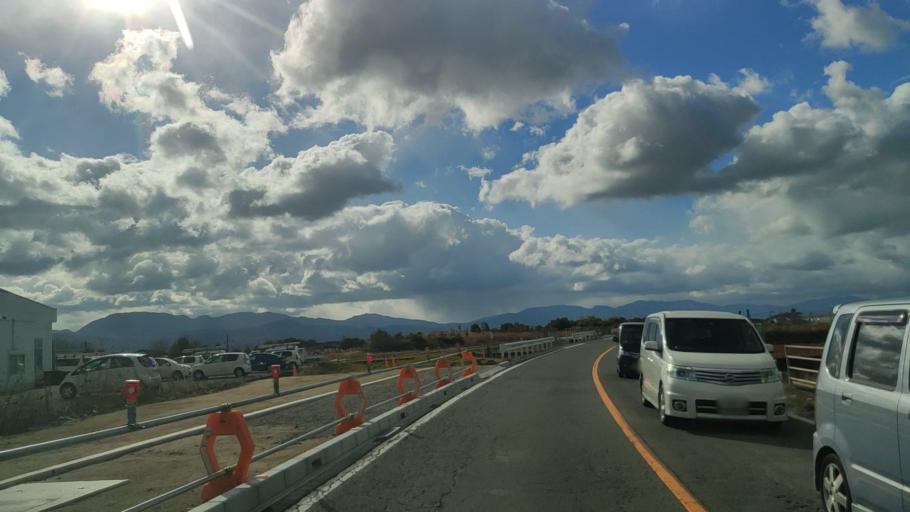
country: JP
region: Ehime
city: Masaki-cho
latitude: 33.8201
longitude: 132.7133
